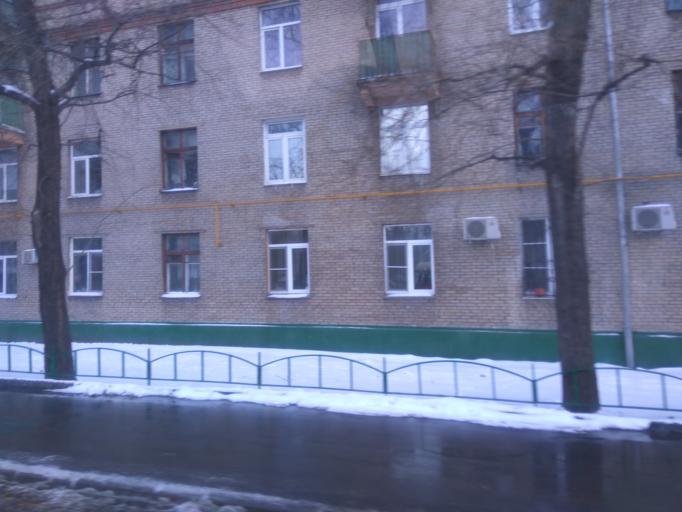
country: RU
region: Moscow
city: Mar'ina Roshcha
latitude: 55.8049
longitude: 37.5736
